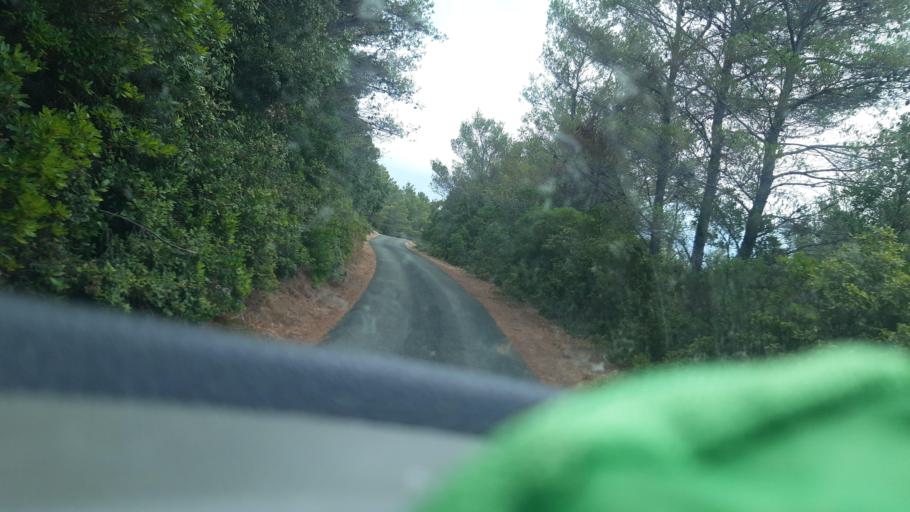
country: HR
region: Dubrovacko-Neretvanska
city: Blato
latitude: 42.7559
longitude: 17.4692
